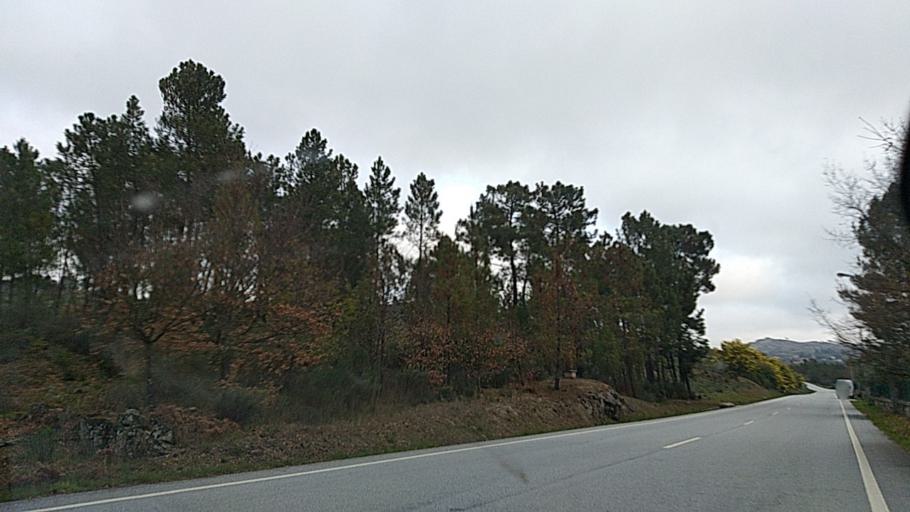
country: PT
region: Guarda
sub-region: Fornos de Algodres
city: Fornos de Algodres
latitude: 40.6407
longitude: -7.4941
